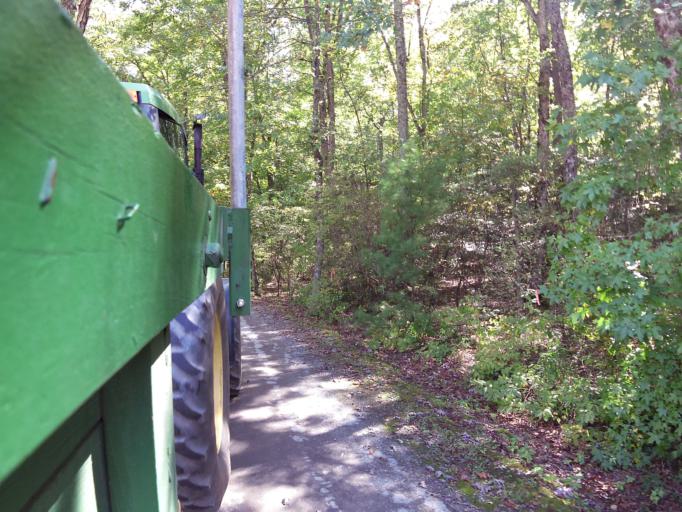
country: US
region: Georgia
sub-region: Dawson County
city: Dawsonville
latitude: 34.5506
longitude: -84.2553
